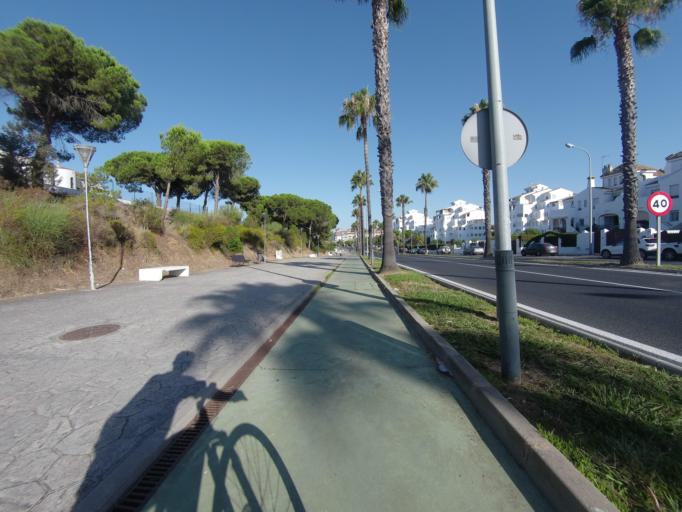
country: ES
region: Andalusia
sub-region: Provincia de Huelva
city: Aljaraque
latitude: 37.2124
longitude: -7.0602
